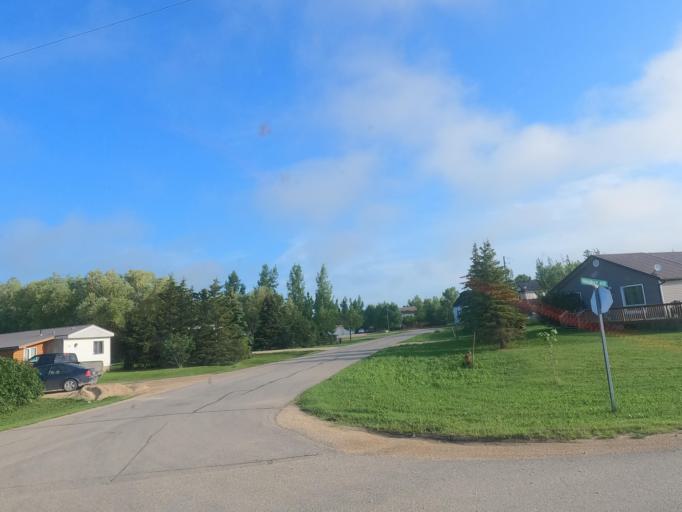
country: CA
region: Manitoba
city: Headingley
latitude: 49.7688
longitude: -97.6216
